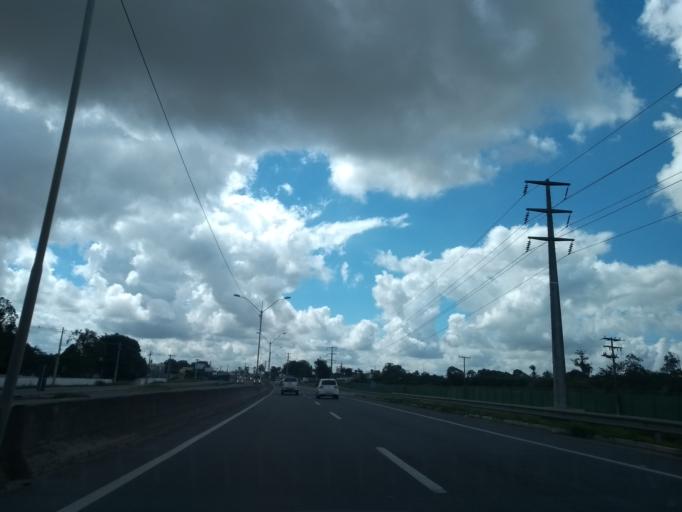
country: BR
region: Bahia
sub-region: Feira De Santana
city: Feira de Santana
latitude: -12.2814
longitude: -38.9442
